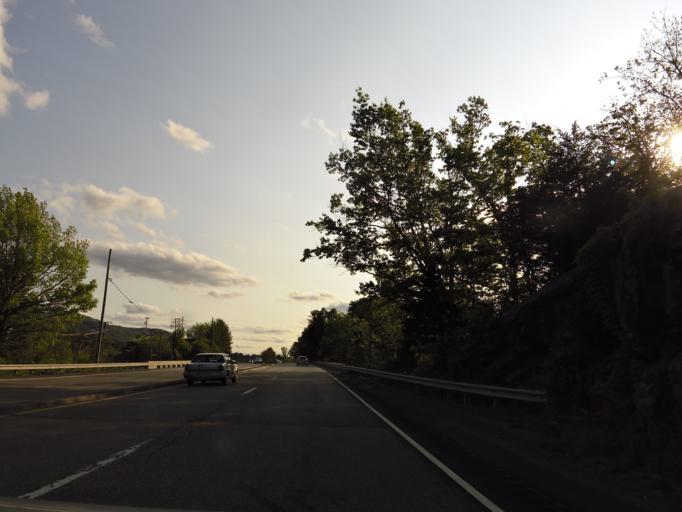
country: US
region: Virginia
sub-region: Tazewell County
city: Claypool Hill
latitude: 37.0794
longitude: -81.7056
